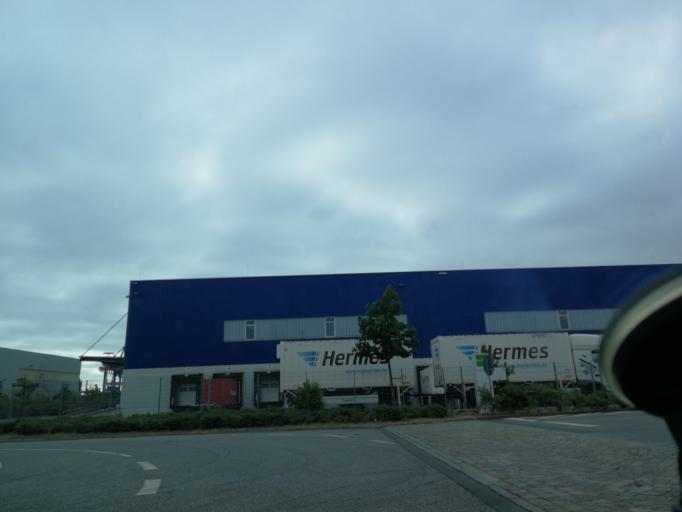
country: DE
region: Hamburg
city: Altona
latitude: 53.5035
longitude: 9.9257
